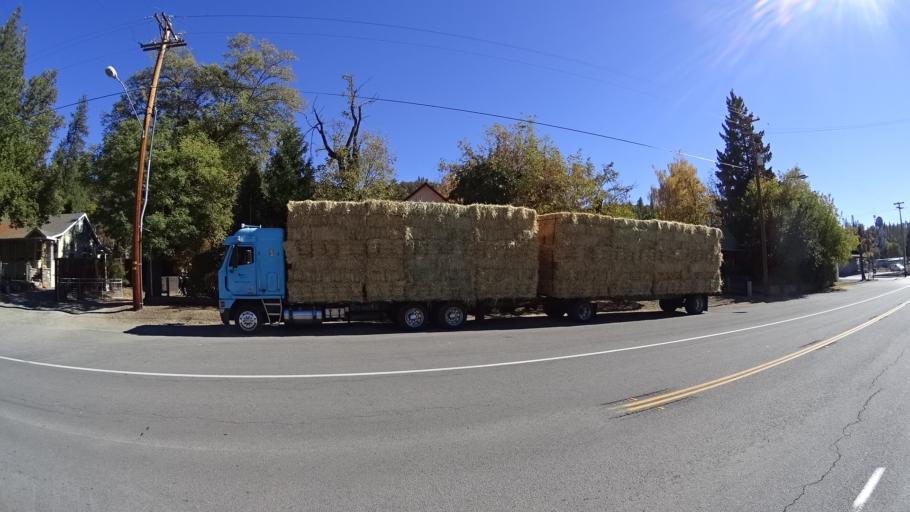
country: US
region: California
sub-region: Siskiyou County
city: Yreka
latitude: 41.6086
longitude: -122.8410
